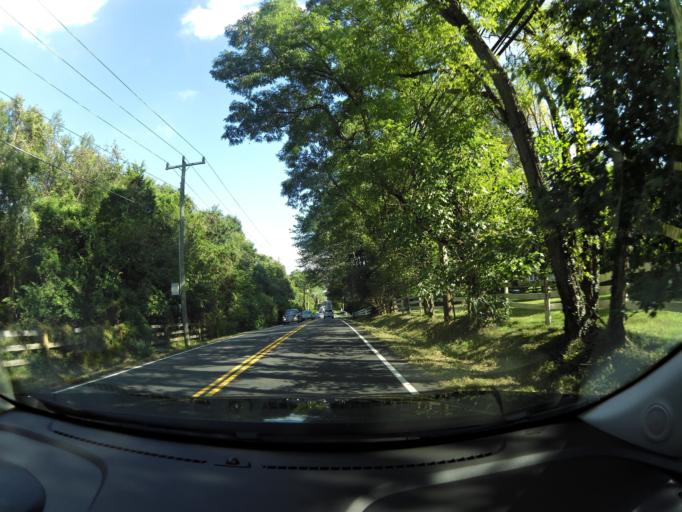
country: US
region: Virginia
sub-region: Fairfax County
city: Great Falls
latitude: 38.9927
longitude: -77.2771
